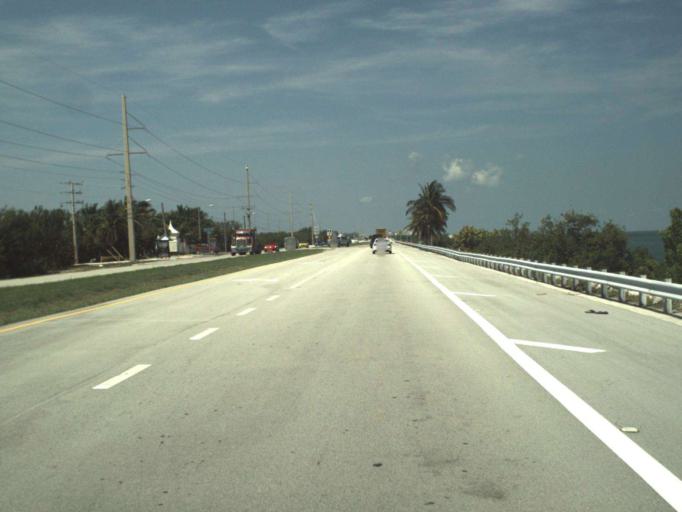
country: US
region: Florida
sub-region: Monroe County
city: Marathon
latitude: 24.7806
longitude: -80.9139
